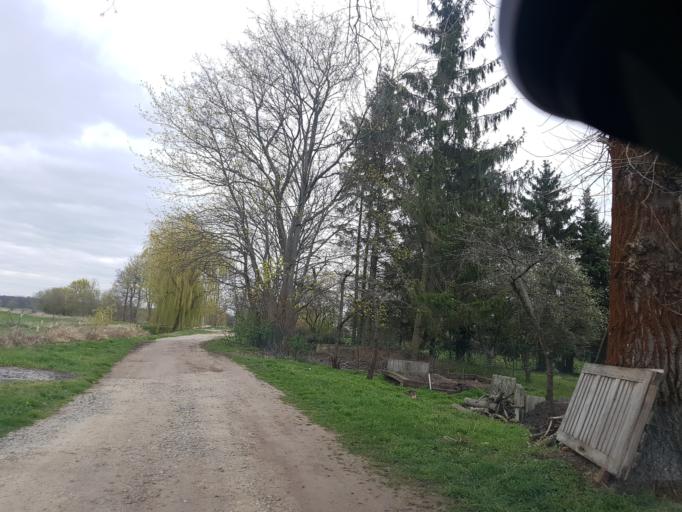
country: DE
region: Brandenburg
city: Bruck
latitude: 52.1982
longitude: 12.7661
